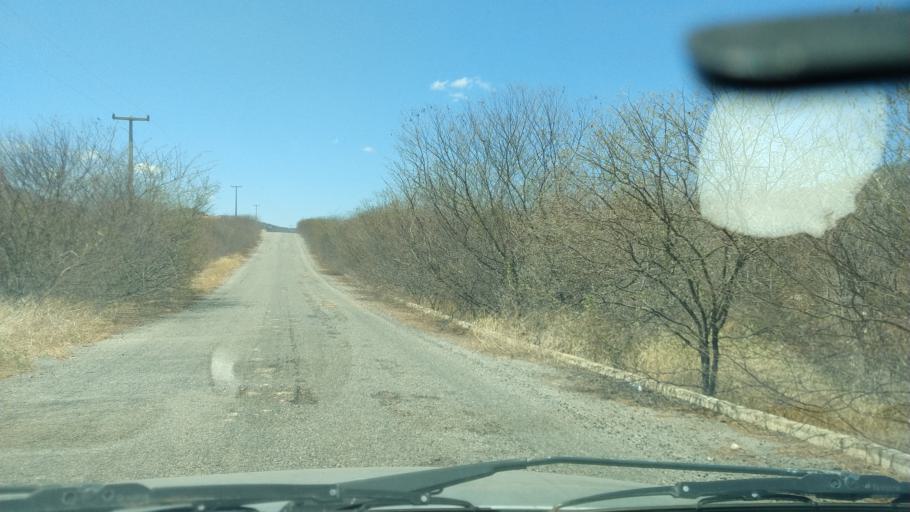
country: BR
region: Rio Grande do Norte
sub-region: Sao Tome
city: Sao Tome
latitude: -5.9759
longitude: -36.1430
